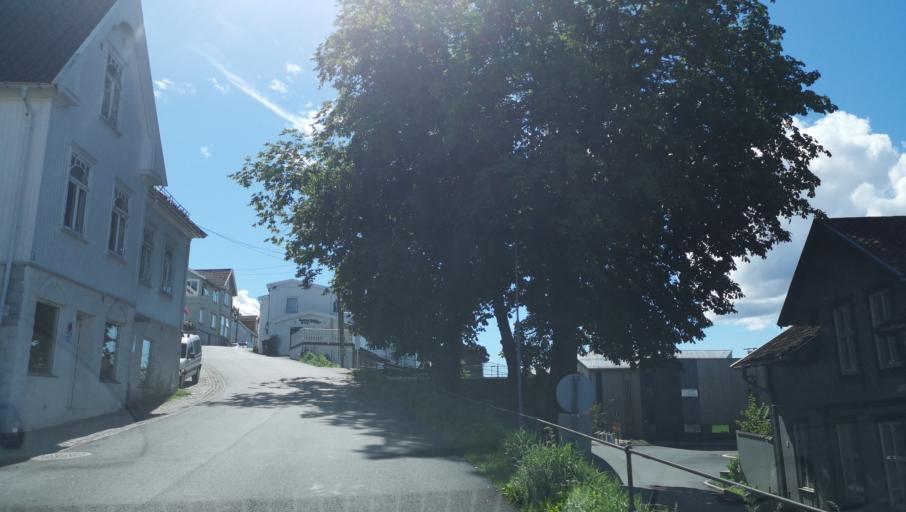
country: NO
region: Akershus
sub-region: Frogn
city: Drobak
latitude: 59.6584
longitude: 10.6306
